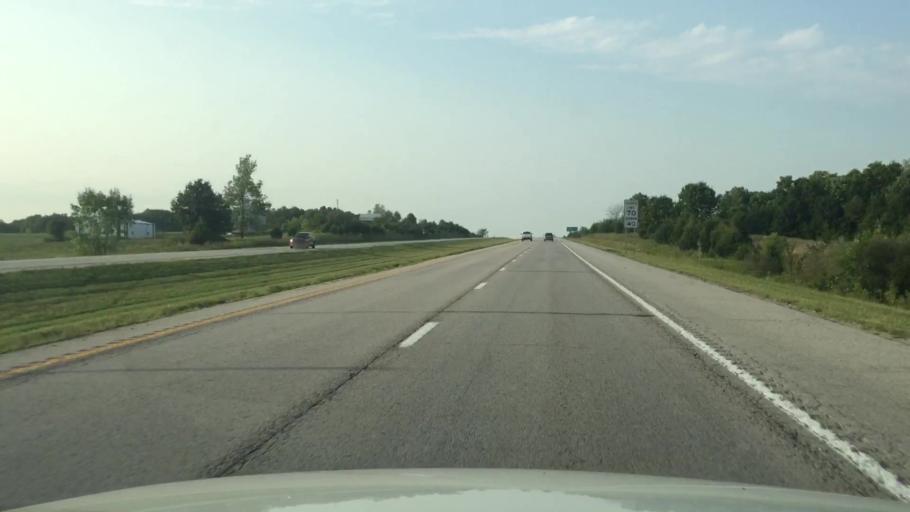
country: US
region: Missouri
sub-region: Harrison County
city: Bethany
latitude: 40.2193
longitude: -94.0129
